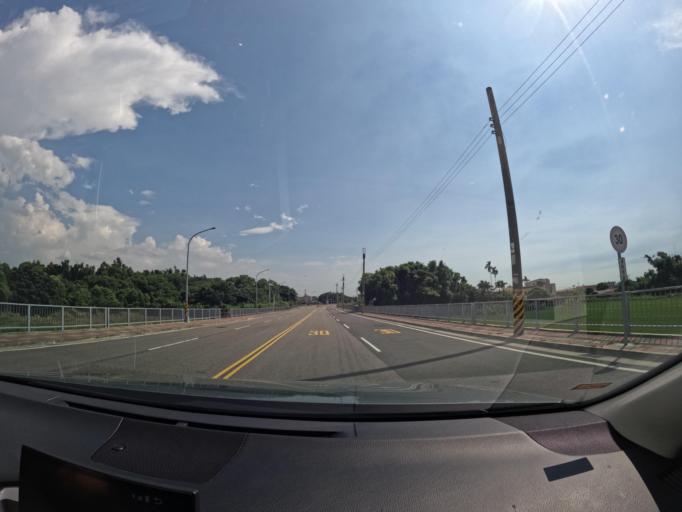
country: TW
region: Taiwan
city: Fengyuan
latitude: 24.2991
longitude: 120.7177
